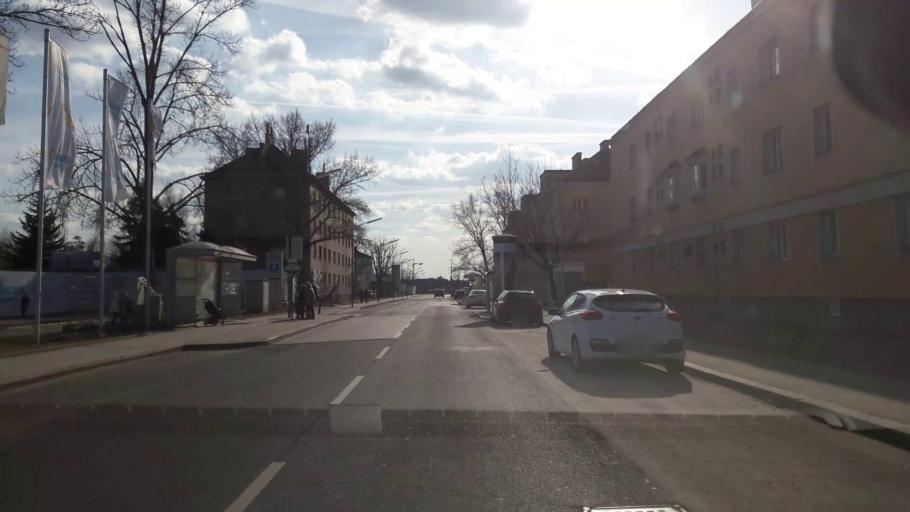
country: AT
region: Lower Austria
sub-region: Politischer Bezirk Wien-Umgebung
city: Schwechat
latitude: 48.1695
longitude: 16.4708
